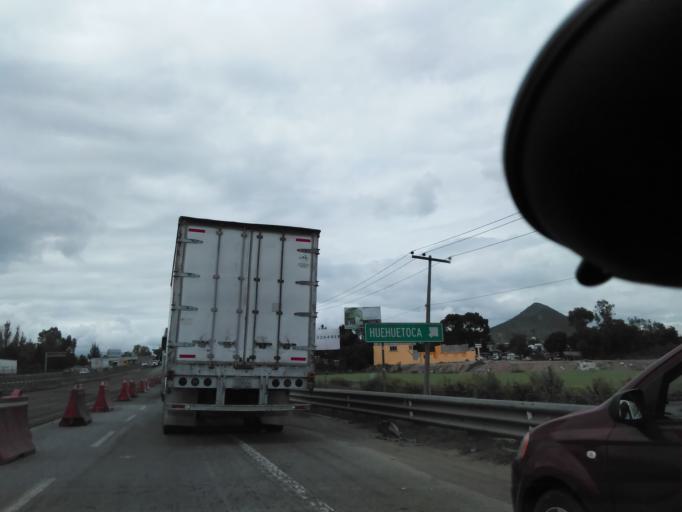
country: MX
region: Mexico
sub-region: Huehuetoca
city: Jorobas
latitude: 19.8226
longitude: -99.2456
